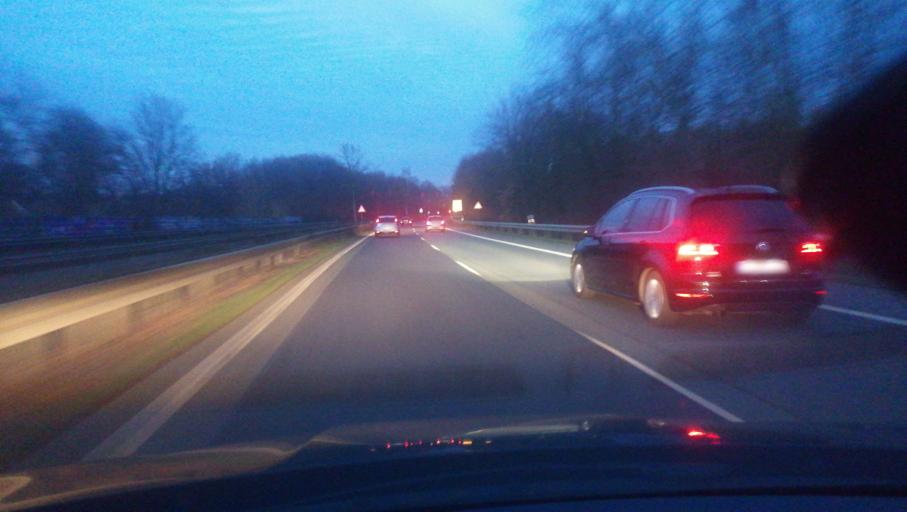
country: DE
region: North Rhine-Westphalia
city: Waltrop
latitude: 51.5537
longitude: 7.3992
